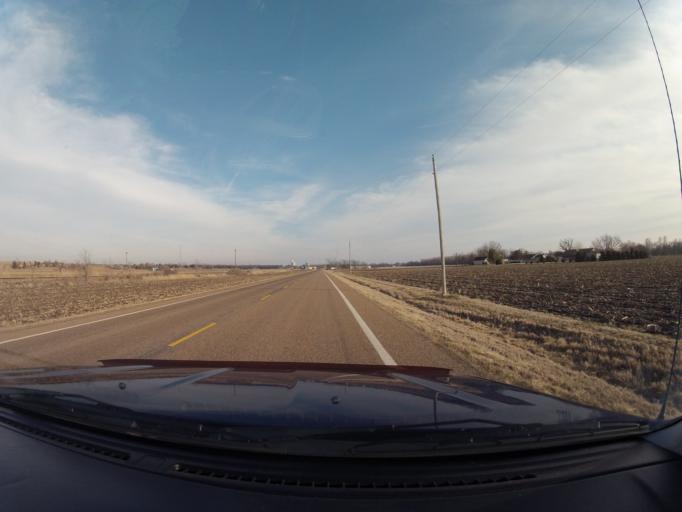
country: US
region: Kansas
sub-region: Pottawatomie County
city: Saint Marys
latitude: 39.2031
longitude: -96.0930
